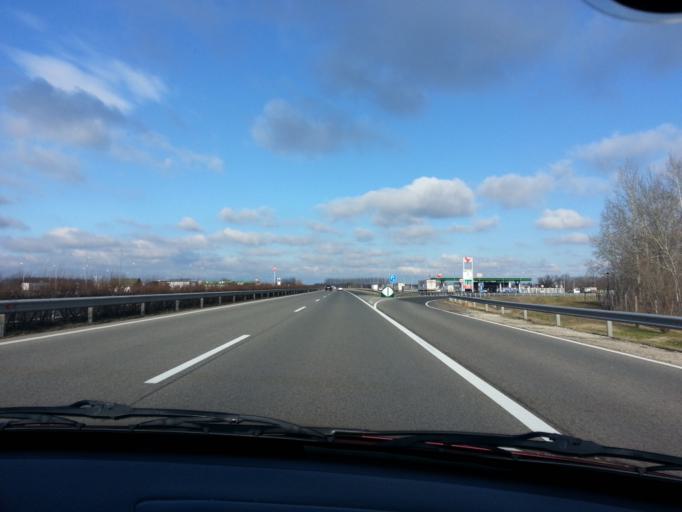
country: HU
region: Csongrad
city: Szatymaz
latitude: 46.3699
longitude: 19.9990
